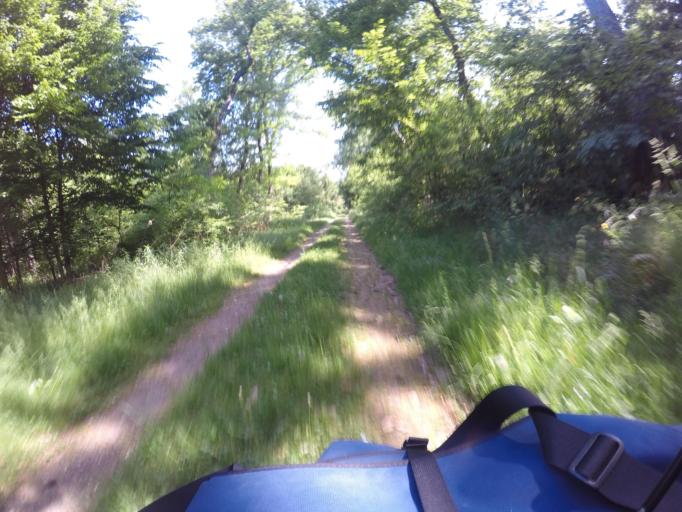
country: DE
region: Baden-Wuerttemberg
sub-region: Karlsruhe Region
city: Rheinstetten
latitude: 48.9419
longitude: 8.3136
